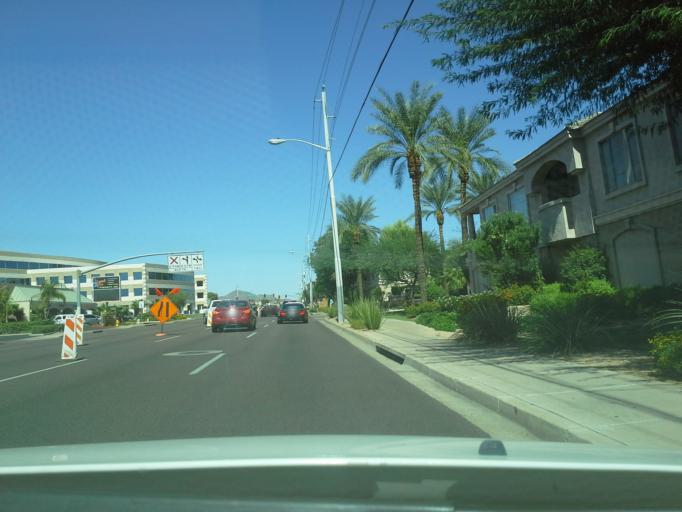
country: US
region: Arizona
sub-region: Maricopa County
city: Phoenix
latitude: 33.5140
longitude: -112.0649
